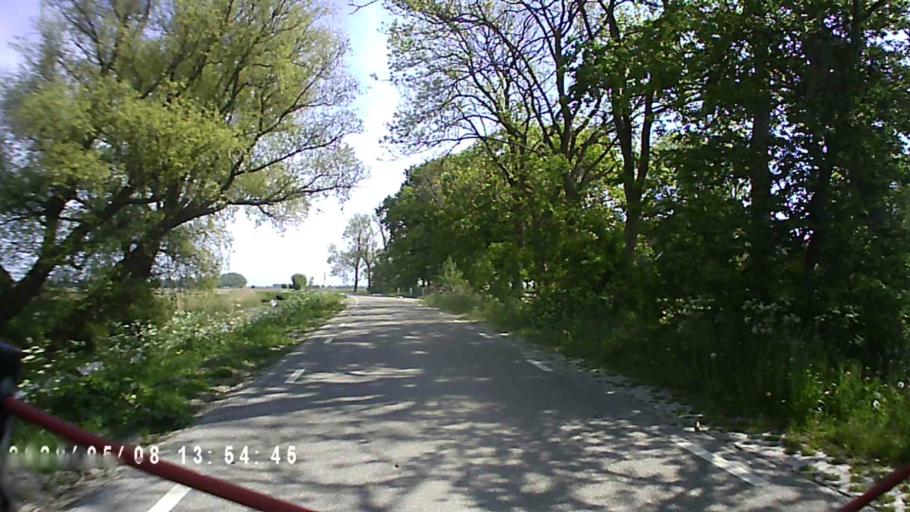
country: NL
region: Groningen
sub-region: Gemeente Appingedam
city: Appingedam
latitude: 53.3363
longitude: 6.7888
